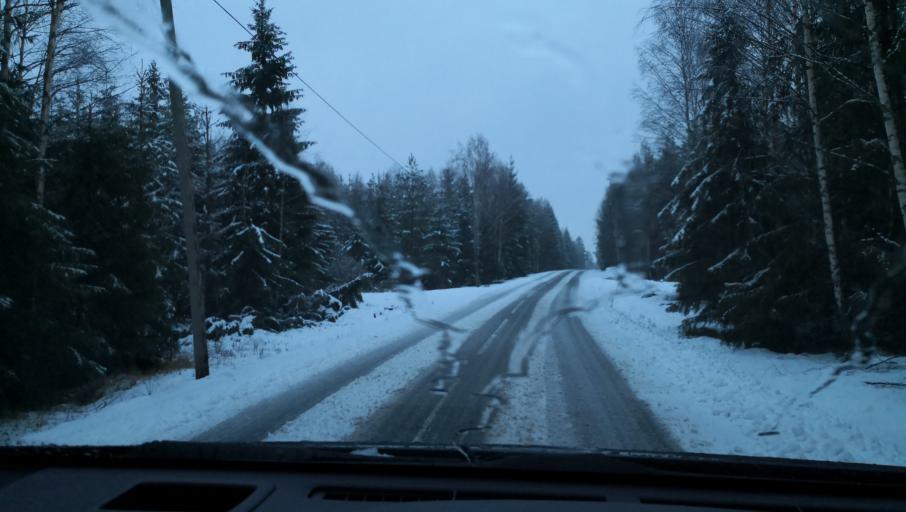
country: SE
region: Vaestmanland
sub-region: Kopings Kommun
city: Kolsva
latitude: 59.5790
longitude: 15.8023
